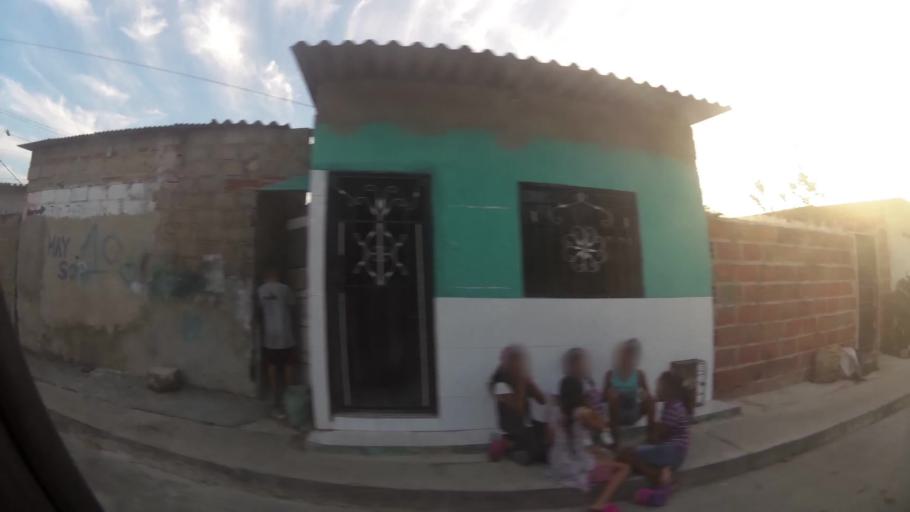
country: CO
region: Atlantico
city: Barranquilla
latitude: 10.9524
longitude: -74.8244
